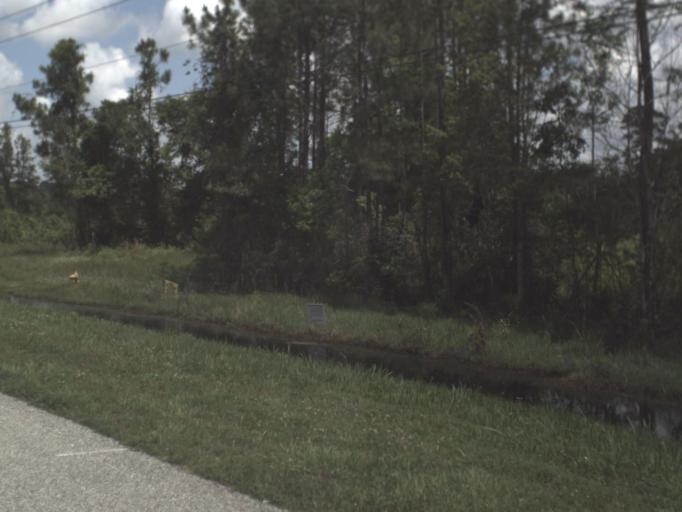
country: US
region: Florida
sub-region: Saint Johns County
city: Palm Valley
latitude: 30.1278
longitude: -81.5022
